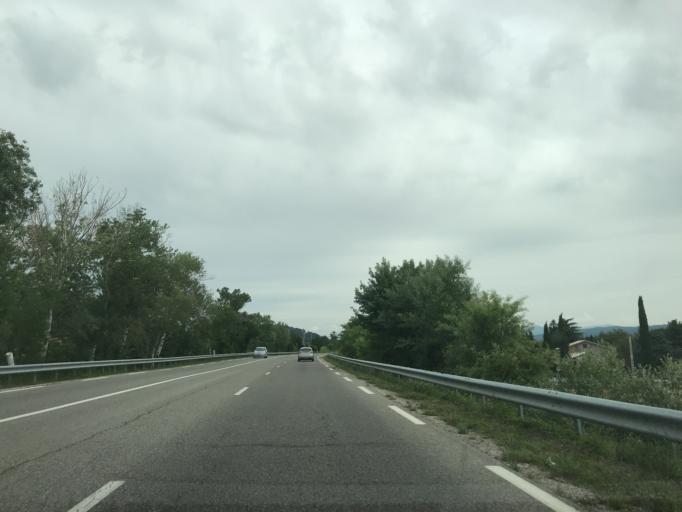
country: FR
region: Provence-Alpes-Cote d'Azur
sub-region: Departement des Alpes-de-Haute-Provence
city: Oraison
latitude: 43.9516
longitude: 5.8907
